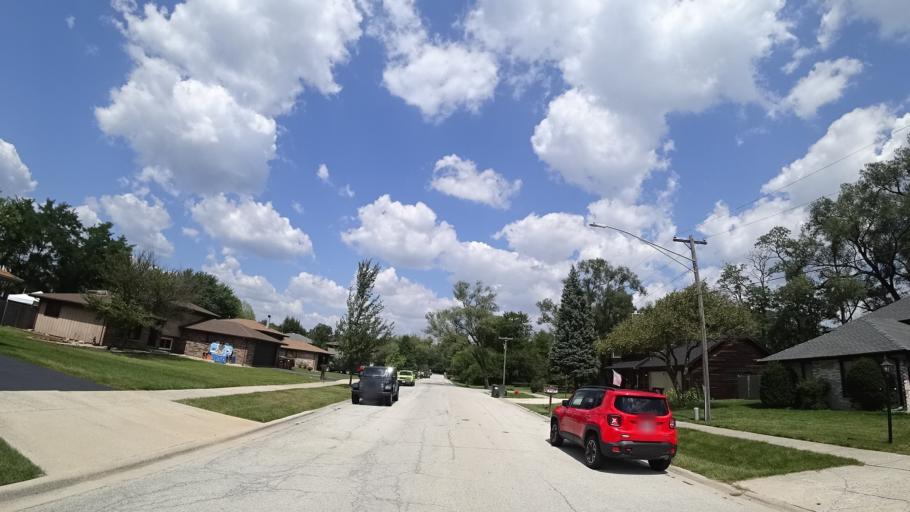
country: US
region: Illinois
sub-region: Cook County
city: Oak Forest
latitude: 41.6250
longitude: -87.7819
